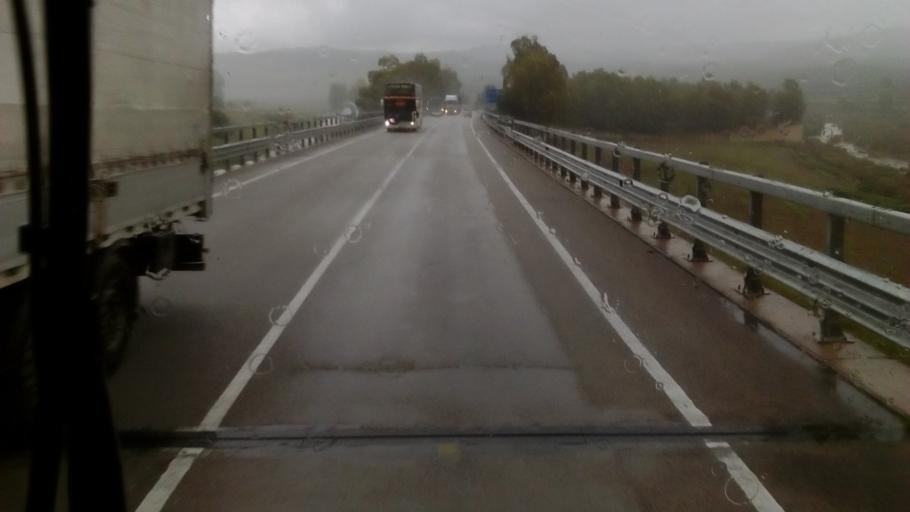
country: IT
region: Sicily
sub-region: Enna
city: Pietraperzia
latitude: 37.4954
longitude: 14.1461
